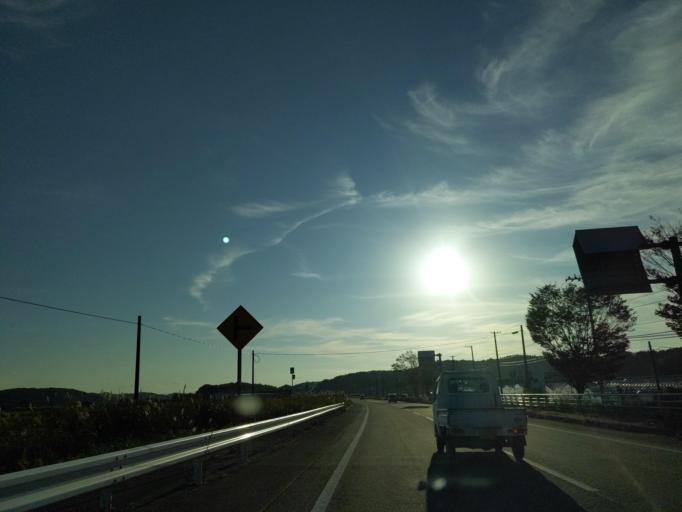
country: JP
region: Niigata
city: Nagaoka
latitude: 37.5763
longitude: 138.7502
